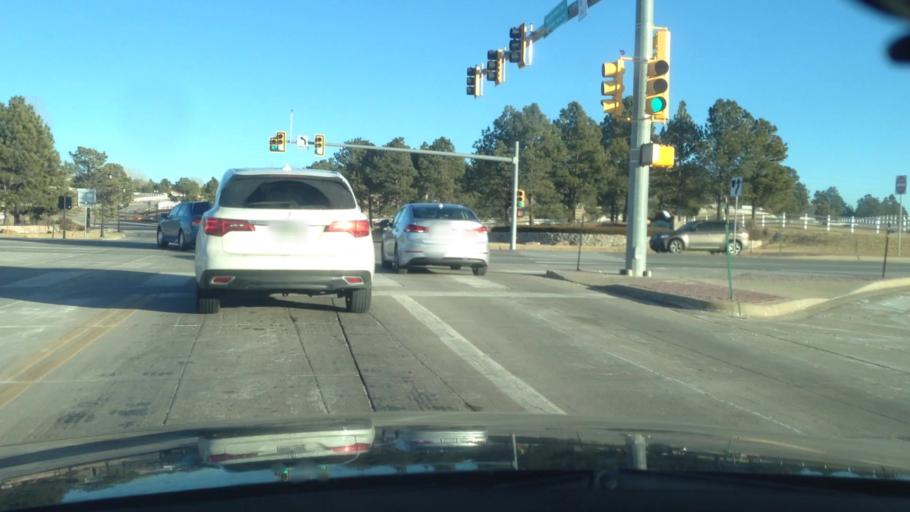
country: US
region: Colorado
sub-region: Douglas County
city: The Pinery
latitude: 39.4404
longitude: -104.7604
